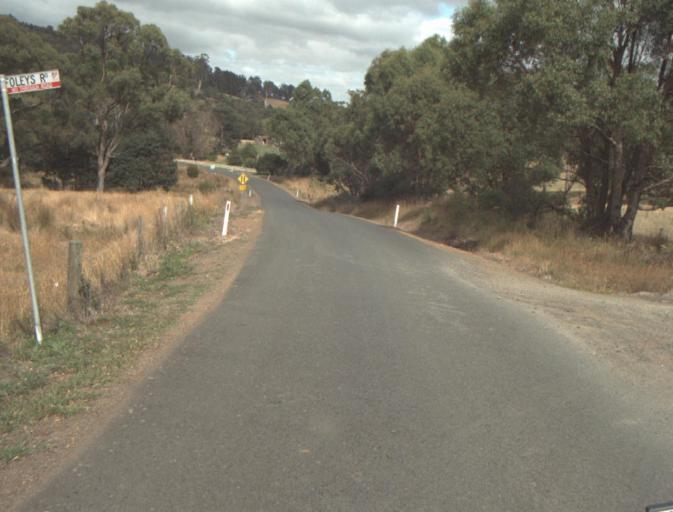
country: AU
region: Tasmania
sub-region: Dorset
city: Scottsdale
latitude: -41.4681
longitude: 147.5754
